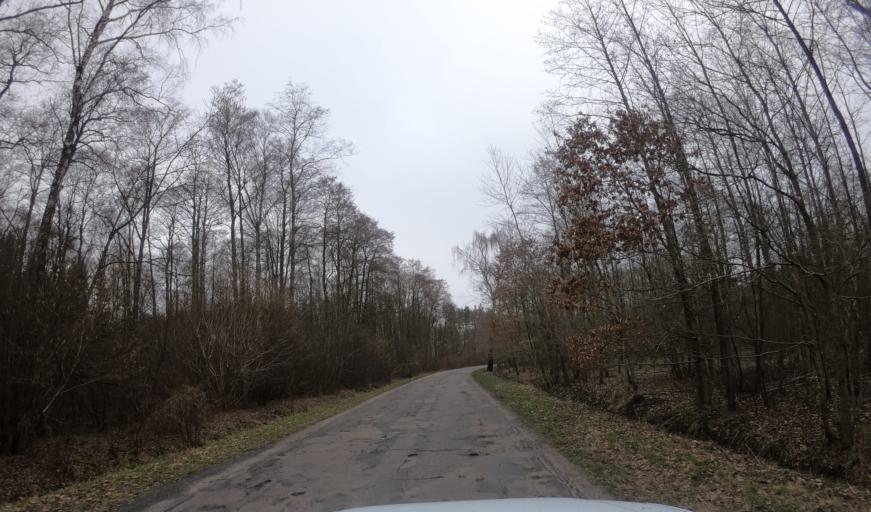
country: PL
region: West Pomeranian Voivodeship
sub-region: Powiat gryficki
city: Gryfice
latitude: 53.8980
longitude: 15.2301
